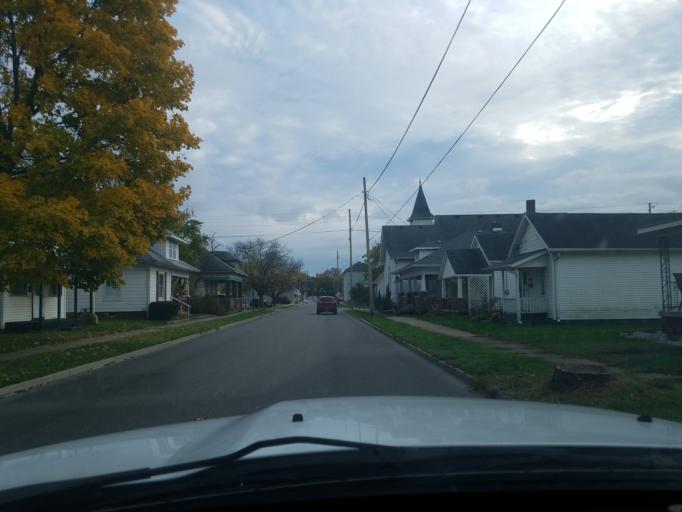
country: US
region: Indiana
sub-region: Shelby County
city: Shelbyville
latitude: 39.5258
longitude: -85.7676
